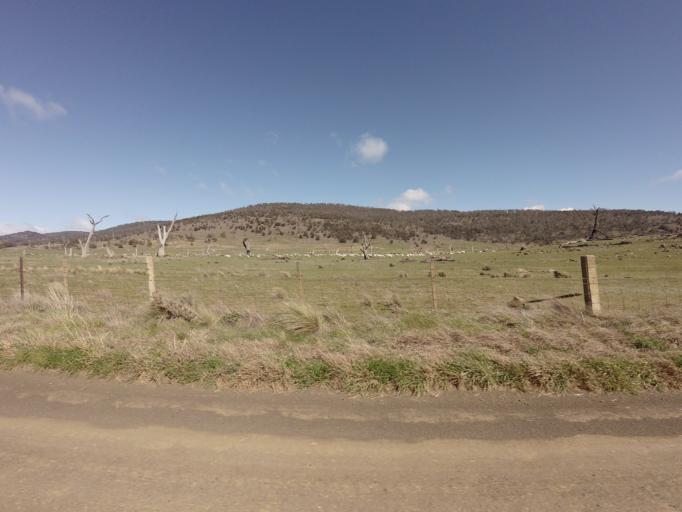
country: AU
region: Tasmania
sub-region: Northern Midlands
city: Evandale
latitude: -41.9256
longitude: 147.4090
